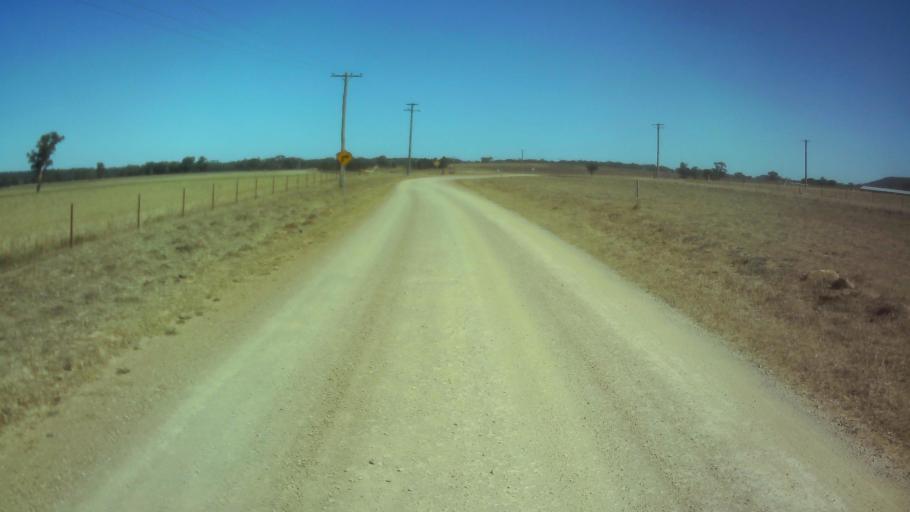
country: AU
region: New South Wales
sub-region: Weddin
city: Grenfell
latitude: -33.9381
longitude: 148.2866
